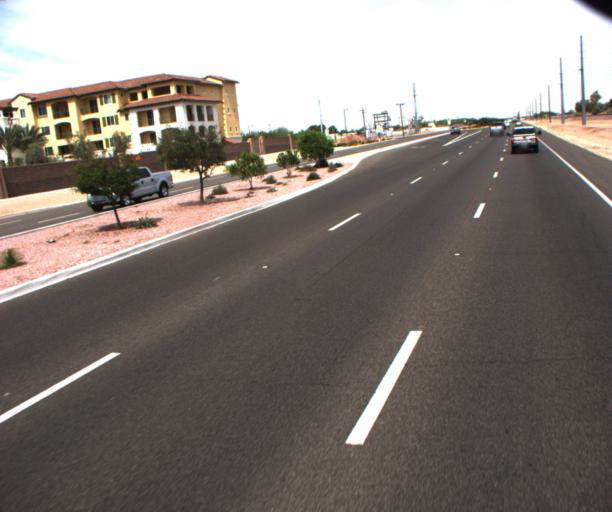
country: US
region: Arizona
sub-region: Maricopa County
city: Sun City West
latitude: 33.6595
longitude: -112.3767
